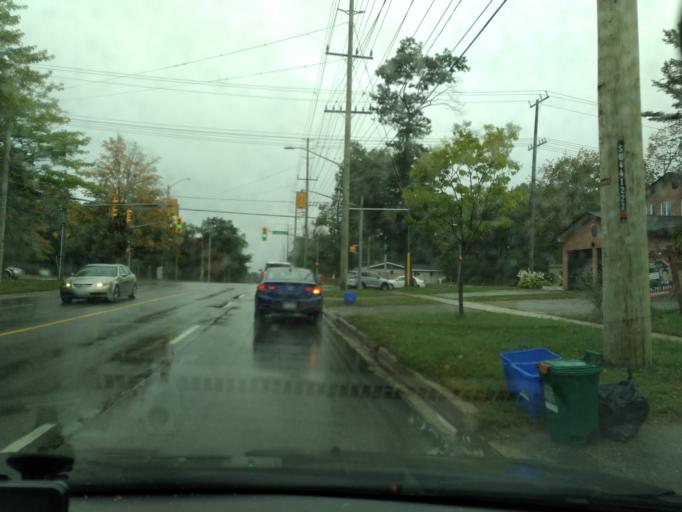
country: CA
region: Ontario
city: Barrie
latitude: 44.3984
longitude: -79.7189
